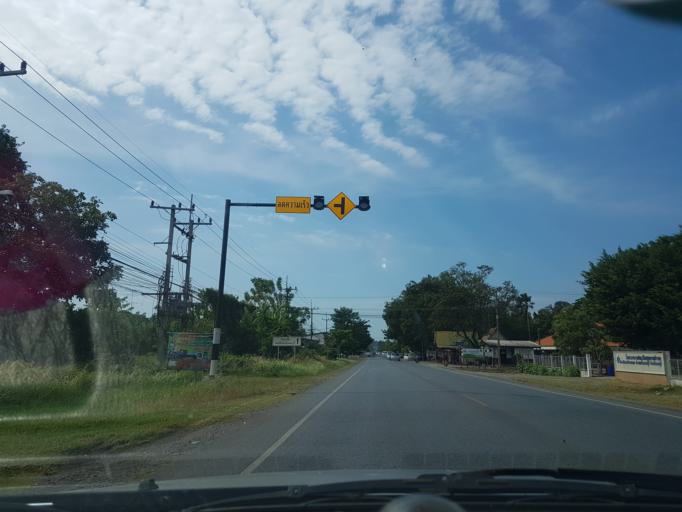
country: TH
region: Lop Buri
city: Lop Buri
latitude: 14.8010
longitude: 100.7374
